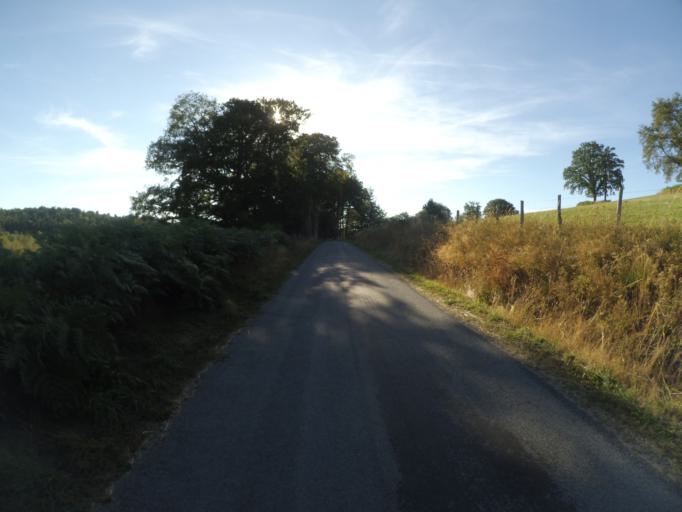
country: FR
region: Limousin
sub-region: Departement de la Creuse
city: Banize
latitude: 45.7465
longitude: 2.0290
